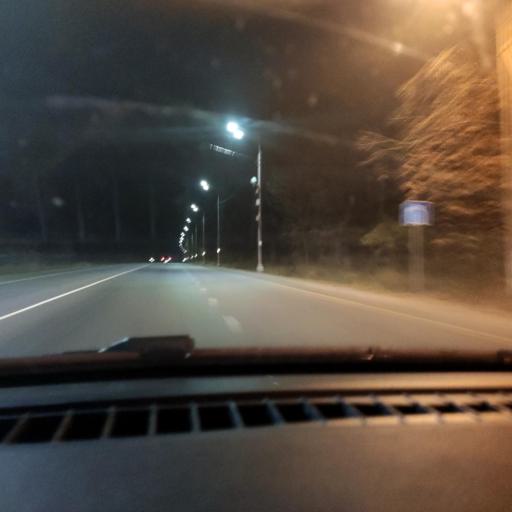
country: RU
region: Voronezj
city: Semiluki
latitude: 51.6389
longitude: 39.0089
